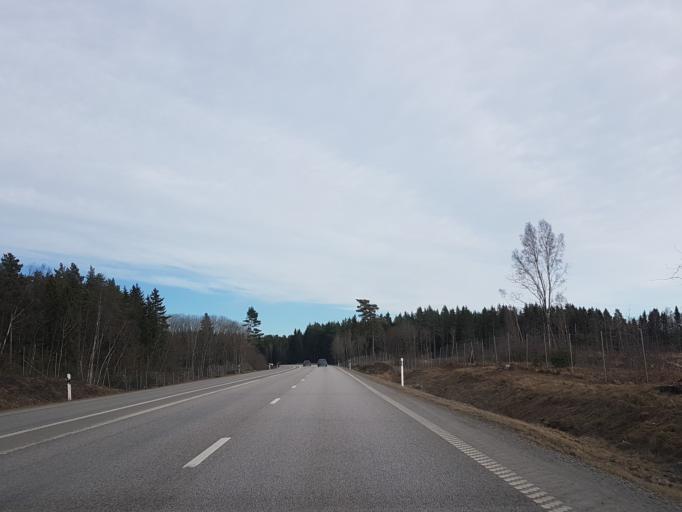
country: SE
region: Stockholm
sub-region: Norrtalje Kommun
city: Norrtalje
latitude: 59.7391
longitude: 18.7239
